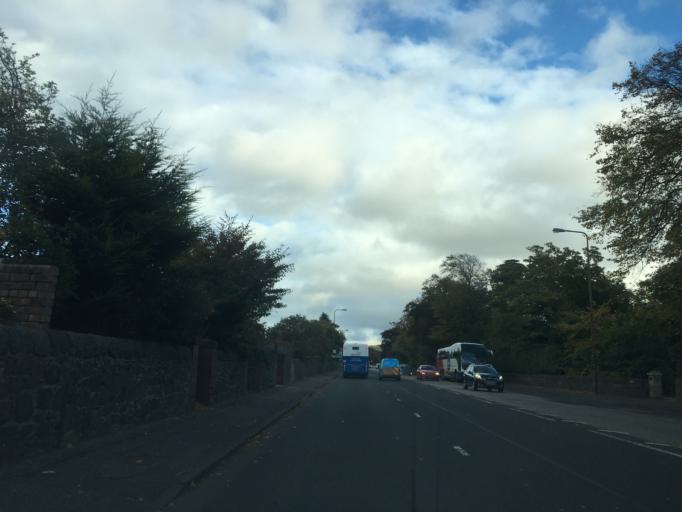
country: GB
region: Scotland
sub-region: Edinburgh
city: Currie
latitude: 55.9612
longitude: -3.3109
